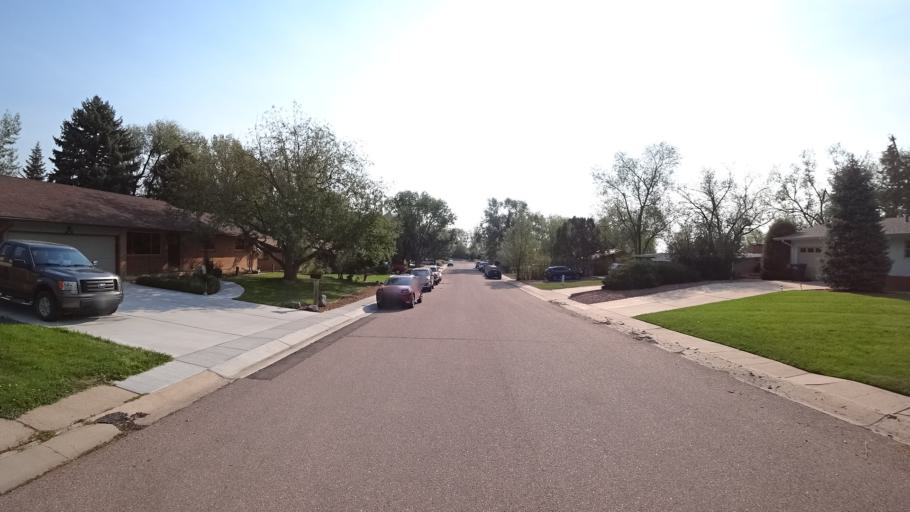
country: US
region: Colorado
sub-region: El Paso County
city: Colorado Springs
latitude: 38.8133
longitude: -104.8478
